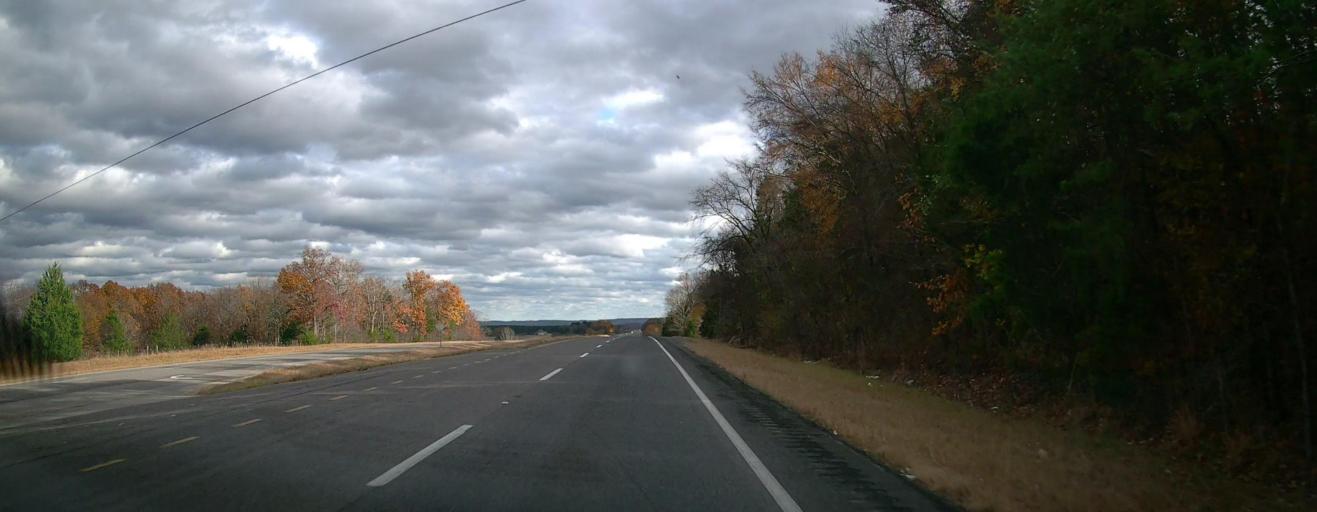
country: US
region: Alabama
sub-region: Morgan County
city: Danville
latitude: 34.3976
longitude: -87.1267
